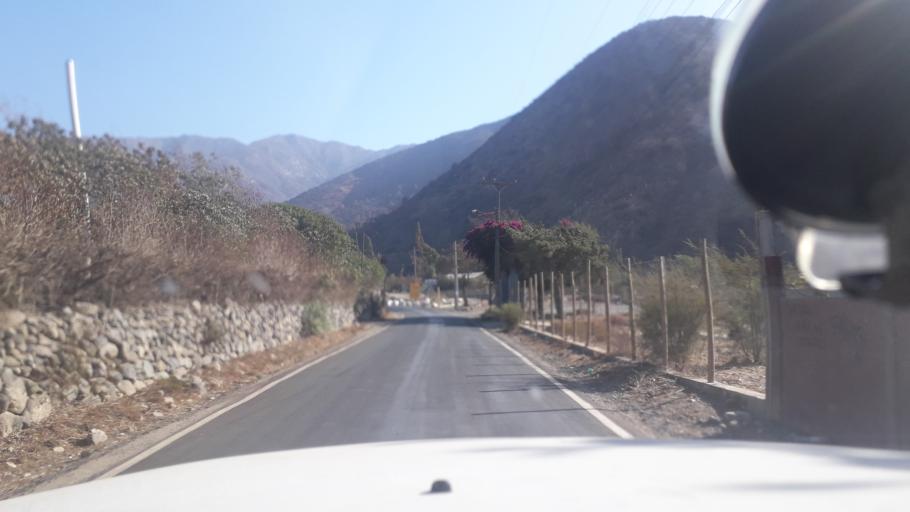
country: CL
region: Valparaiso
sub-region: Provincia de Marga Marga
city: Limache
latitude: -33.0534
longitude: -71.1110
